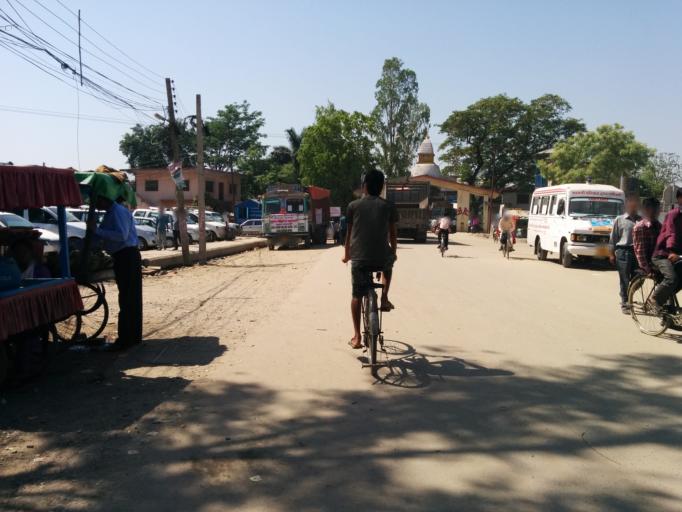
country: NP
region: Western Region
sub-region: Lumbini Zone
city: Bhairahawa
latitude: 27.4770
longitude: 83.4699
